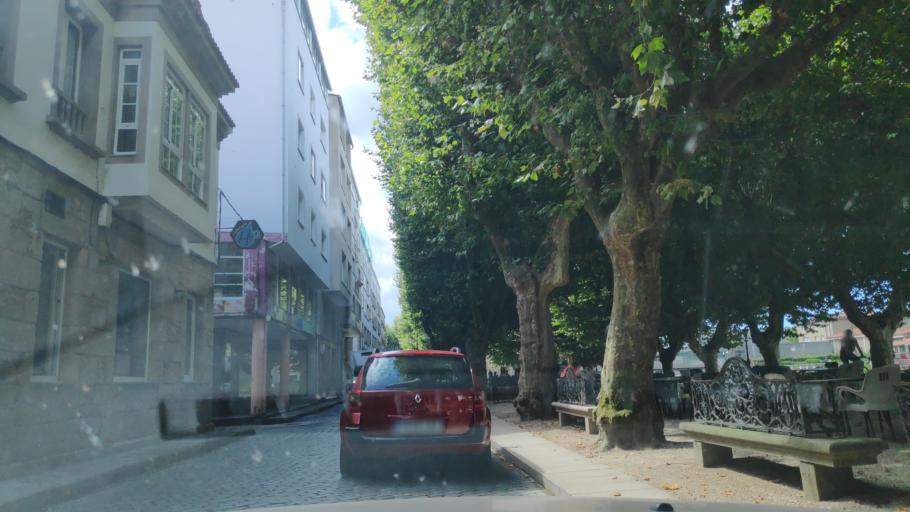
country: ES
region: Galicia
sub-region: Provincia da Coruna
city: Padron
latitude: 42.7380
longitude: -8.6615
